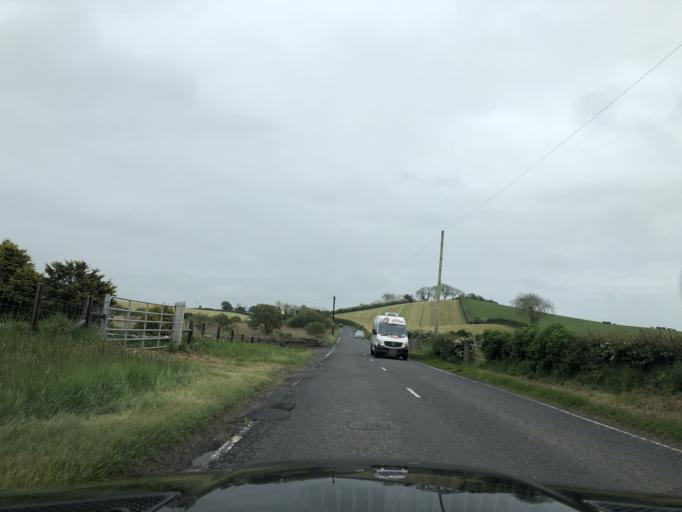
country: GB
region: Northern Ireland
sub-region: Down District
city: Portaferry
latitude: 54.3572
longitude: -5.5929
